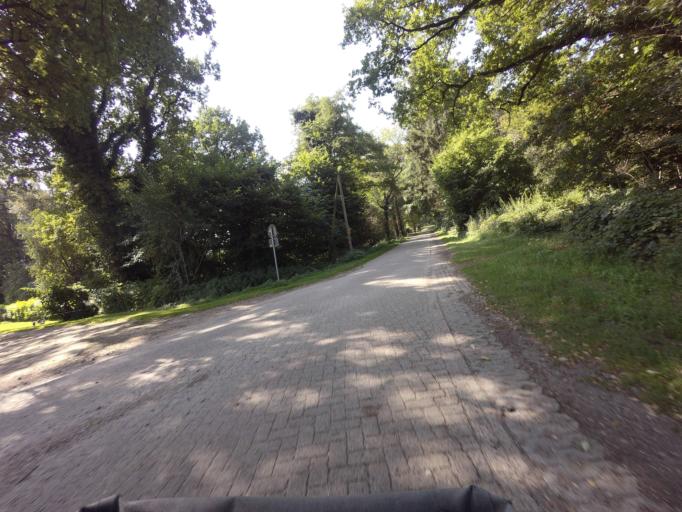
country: DE
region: Lower Saxony
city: Wilsum
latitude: 52.5346
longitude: 6.8285
